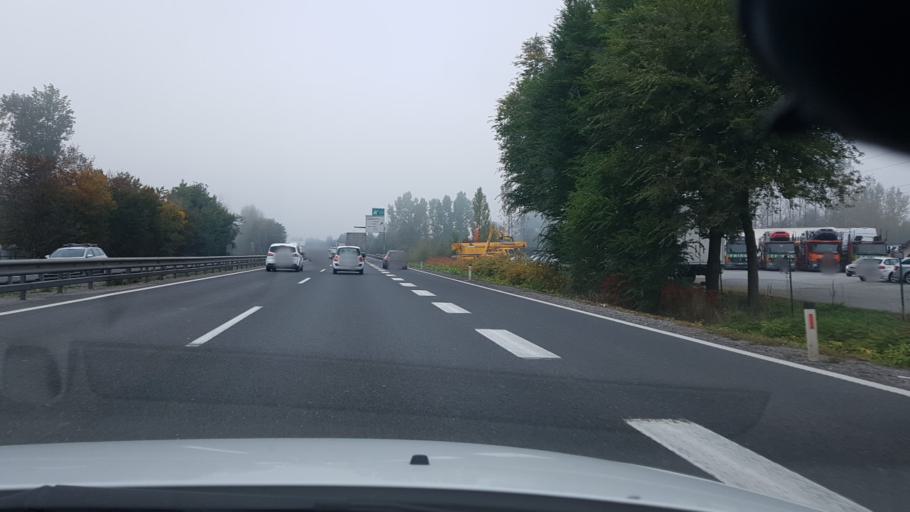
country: SI
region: Ljubljana
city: Ljubljana
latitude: 46.0325
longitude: 14.4714
